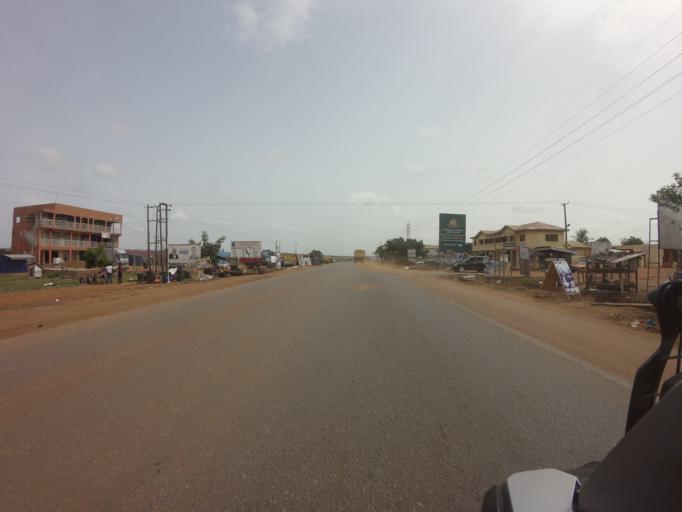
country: GH
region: Greater Accra
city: Tema
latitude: 5.7534
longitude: 0.0456
